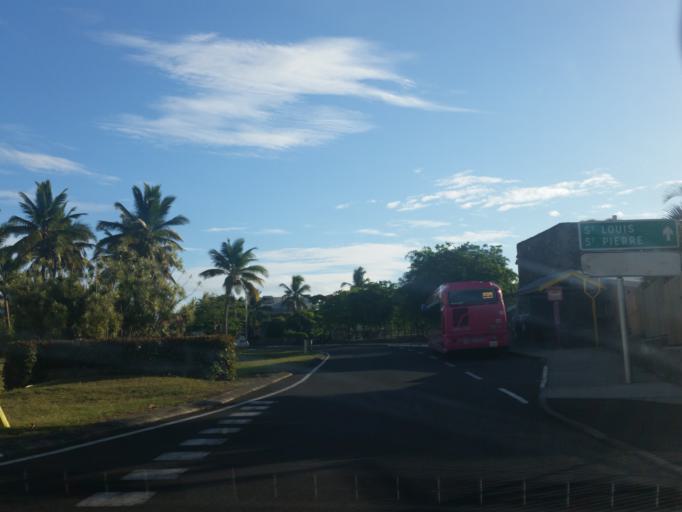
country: RE
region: Reunion
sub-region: Reunion
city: Les Avirons
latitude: -21.2715
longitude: 55.3343
